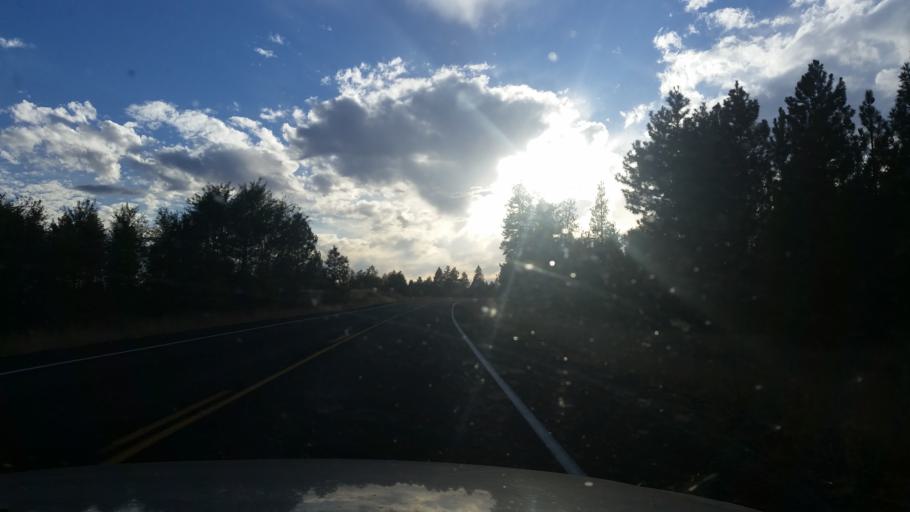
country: US
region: Washington
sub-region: Spokane County
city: Medical Lake
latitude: 47.4381
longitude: -117.7657
